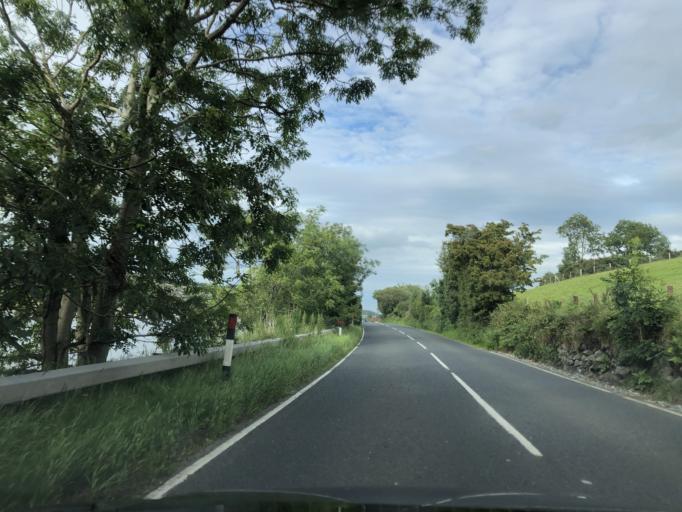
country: GB
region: Northern Ireland
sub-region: Down District
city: Castlewellan
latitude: 54.2378
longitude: -5.9990
